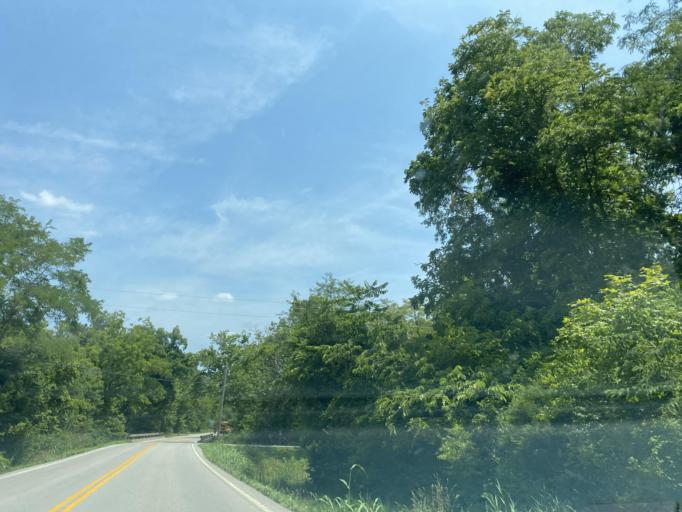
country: US
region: Kentucky
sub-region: Campbell County
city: Claryville
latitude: 38.9272
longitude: -84.4332
